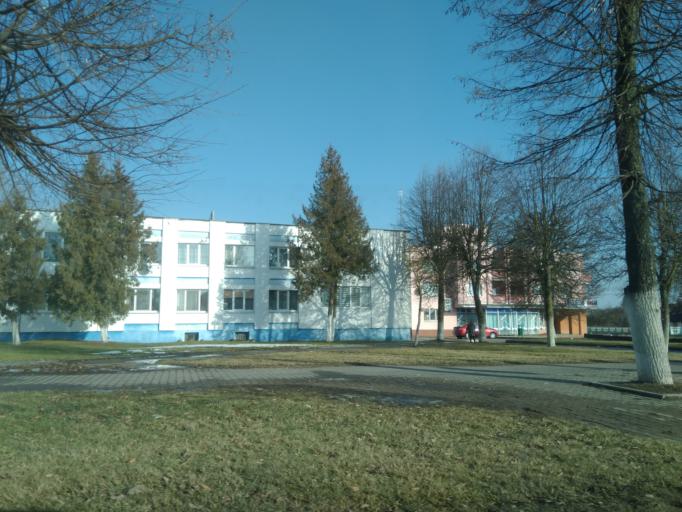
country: BY
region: Minsk
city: Snow
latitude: 53.2184
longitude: 26.4032
